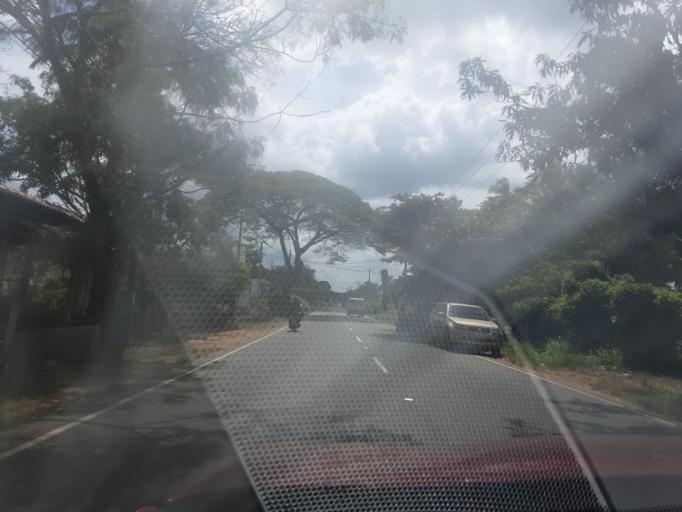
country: LK
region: North Western
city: Kuliyapitiya
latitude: 7.4754
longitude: 80.0118
